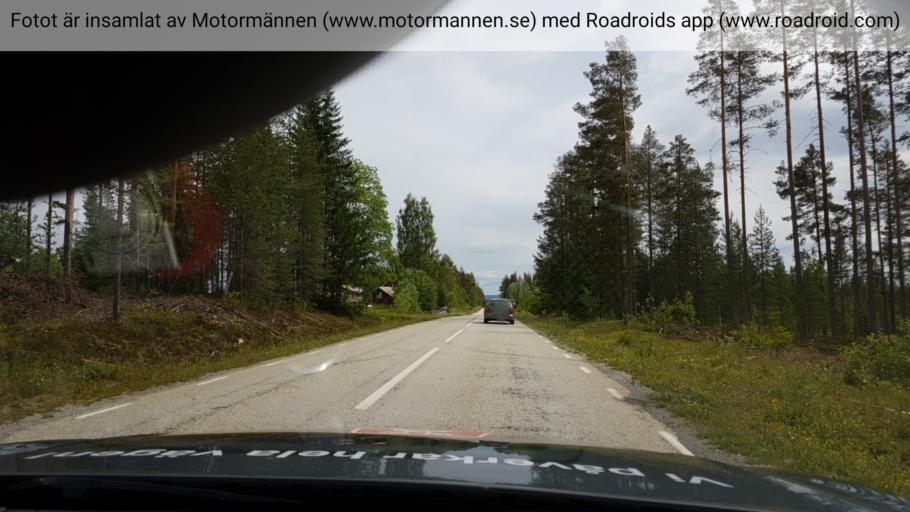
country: SE
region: Jaemtland
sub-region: Bergs Kommun
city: Hoverberg
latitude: 62.6502
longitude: 14.3347
